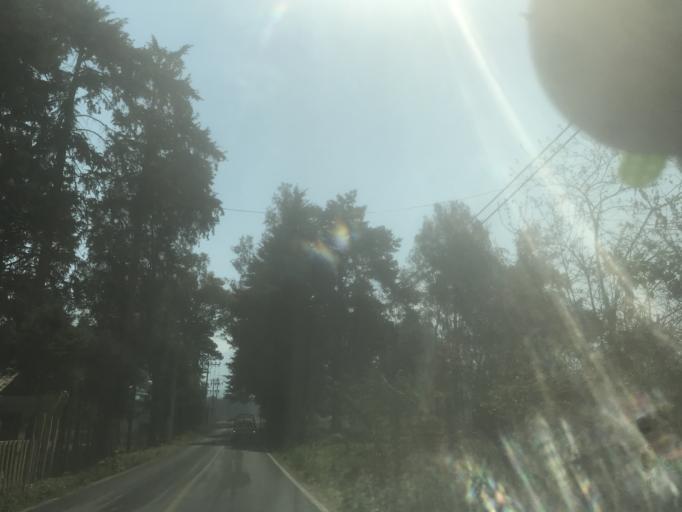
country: MX
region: Mexico
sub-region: Ecatzingo
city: San Marcos Tecomaxusco
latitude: 18.9996
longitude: -98.7693
